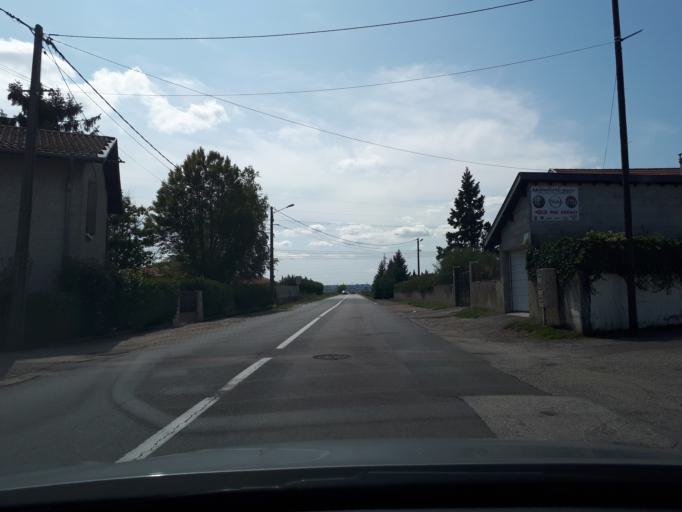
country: FR
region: Rhone-Alpes
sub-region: Departement de l'Isere
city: Chamagnieu
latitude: 45.6673
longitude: 5.1419
